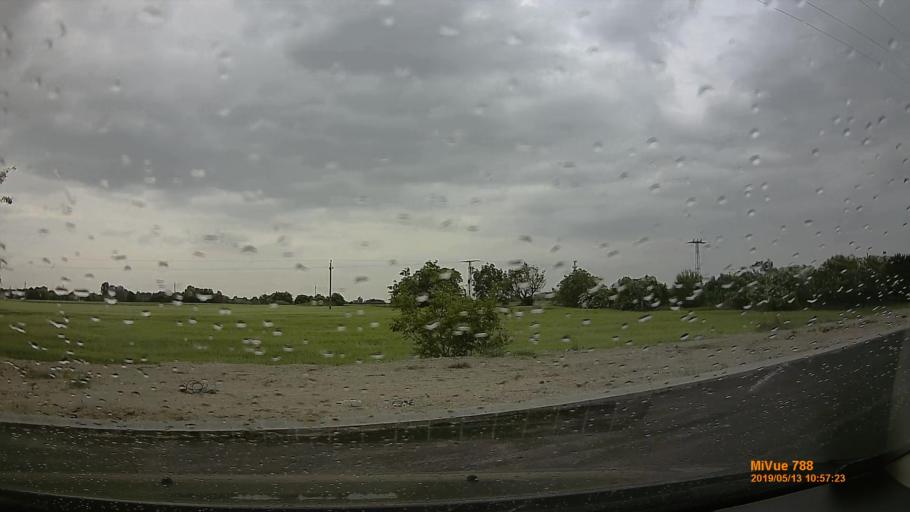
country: HU
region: Budapest
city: Budapest XXIII. keruelet
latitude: 47.3892
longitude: 19.0995
